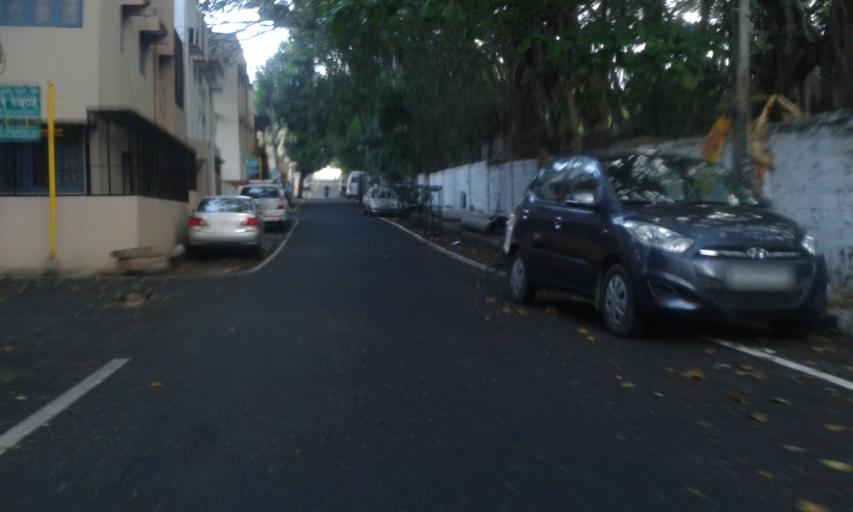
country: IN
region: Karnataka
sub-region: Bangalore Urban
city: Bangalore
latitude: 12.9329
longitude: 77.5886
